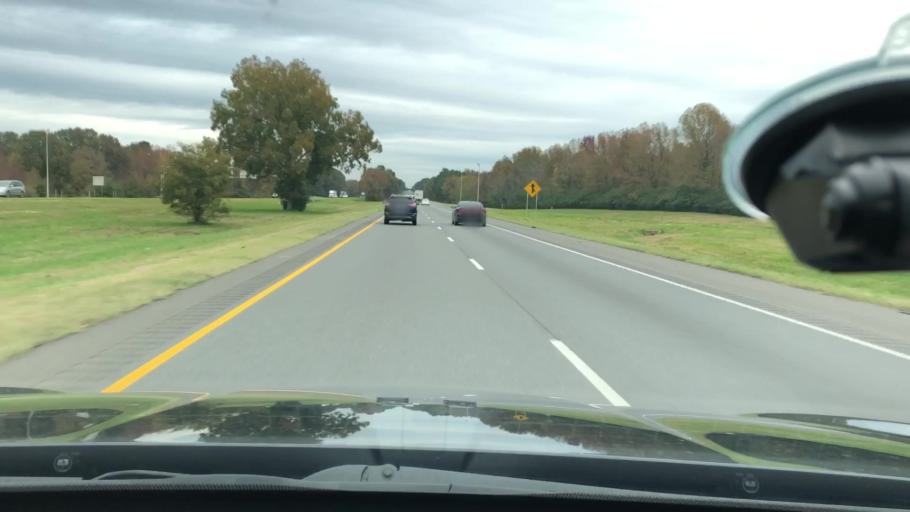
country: US
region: Arkansas
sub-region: Hempstead County
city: Hope
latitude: 33.6922
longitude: -93.5963
